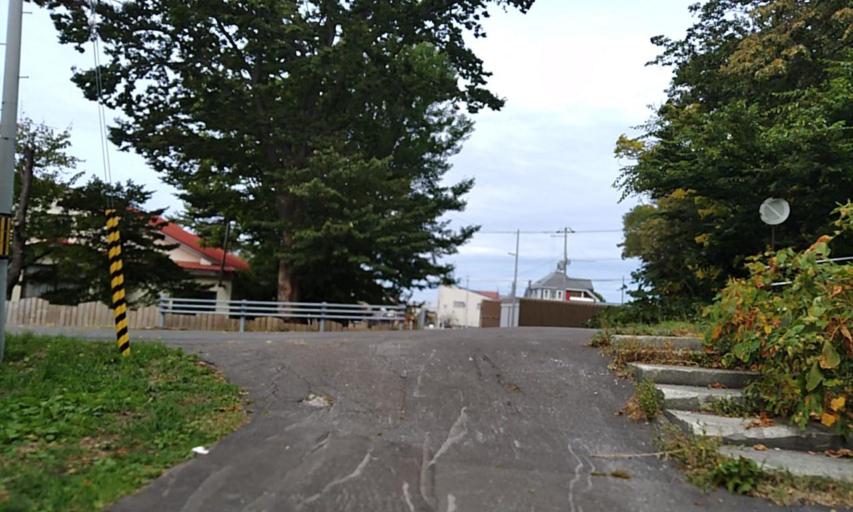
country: JP
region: Hokkaido
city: Rumoi
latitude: 43.8559
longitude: 141.5241
